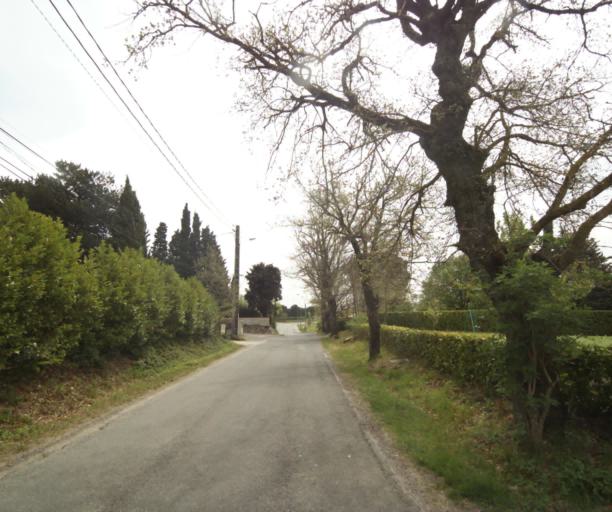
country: FR
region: Midi-Pyrenees
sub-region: Departement de la Haute-Garonne
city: Pechabou
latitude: 43.4998
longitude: 1.5033
